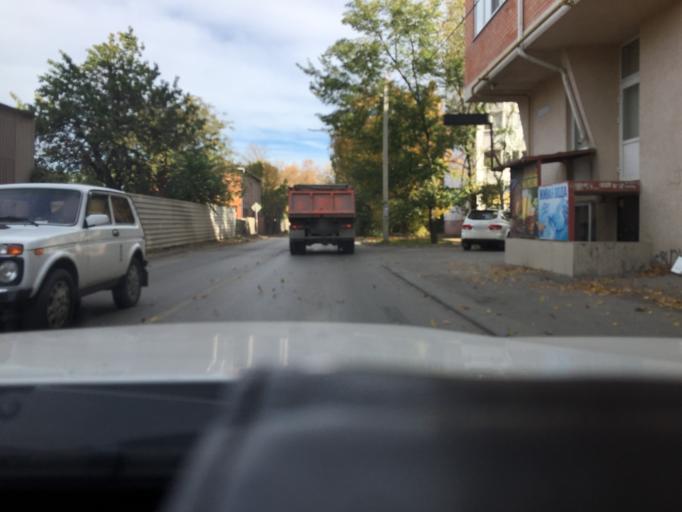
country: RU
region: Rostov
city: Imeni Chkalova
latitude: 47.2813
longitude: 39.7998
